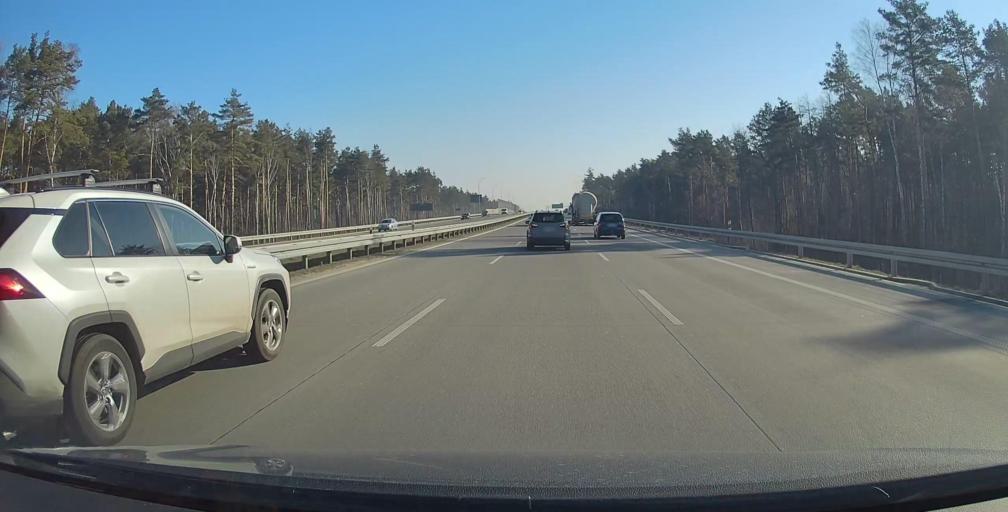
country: PL
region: Masovian Voivodeship
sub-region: Powiat otwocki
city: Jozefow
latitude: 52.1927
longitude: 21.2413
